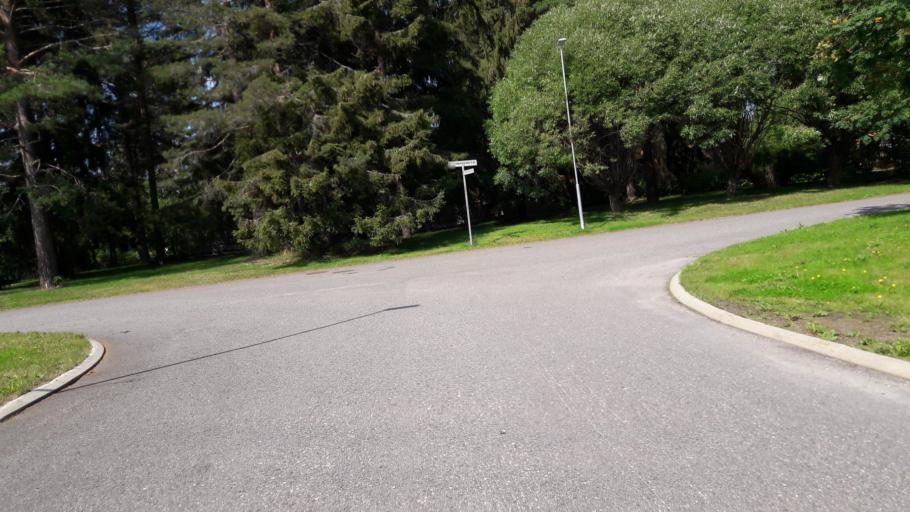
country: FI
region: North Karelia
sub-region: Joensuu
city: Joensuu
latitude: 62.5495
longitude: 29.8317
